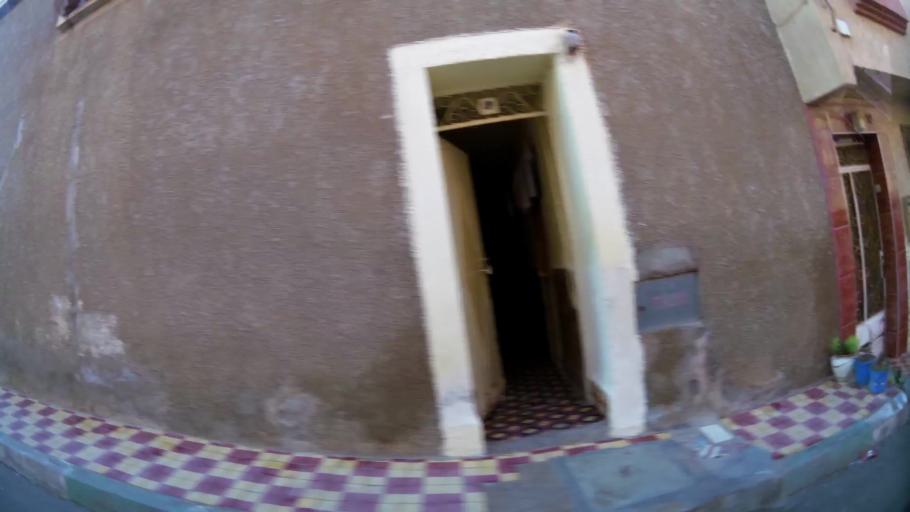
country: MA
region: Oriental
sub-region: Berkane-Taourirt
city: Berkane
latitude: 34.9264
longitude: -2.3210
